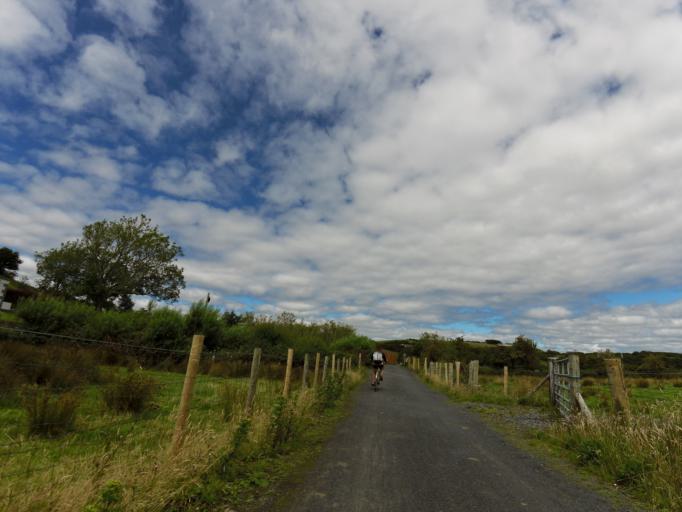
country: IE
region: Connaught
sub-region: Maigh Eo
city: Westport
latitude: 53.8544
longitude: -9.5414
